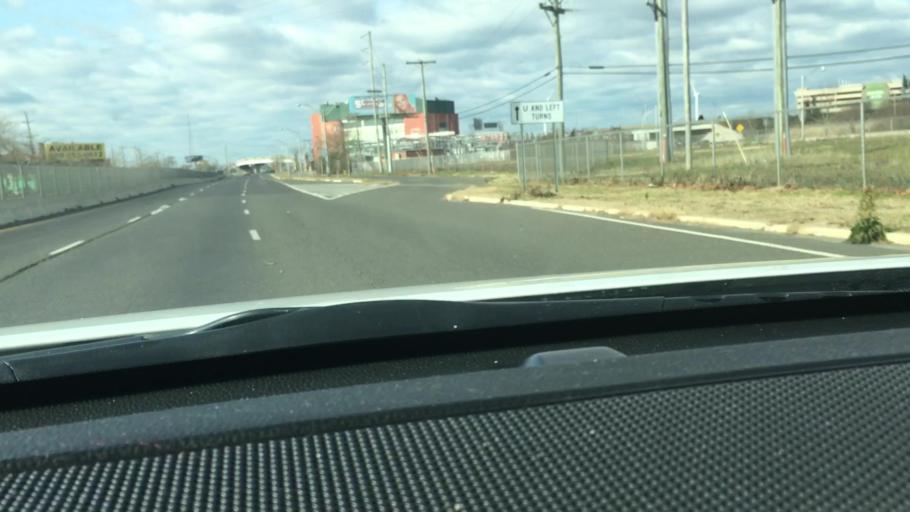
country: US
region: New Jersey
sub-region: Atlantic County
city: Atlantic City
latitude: 39.3716
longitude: -74.4332
